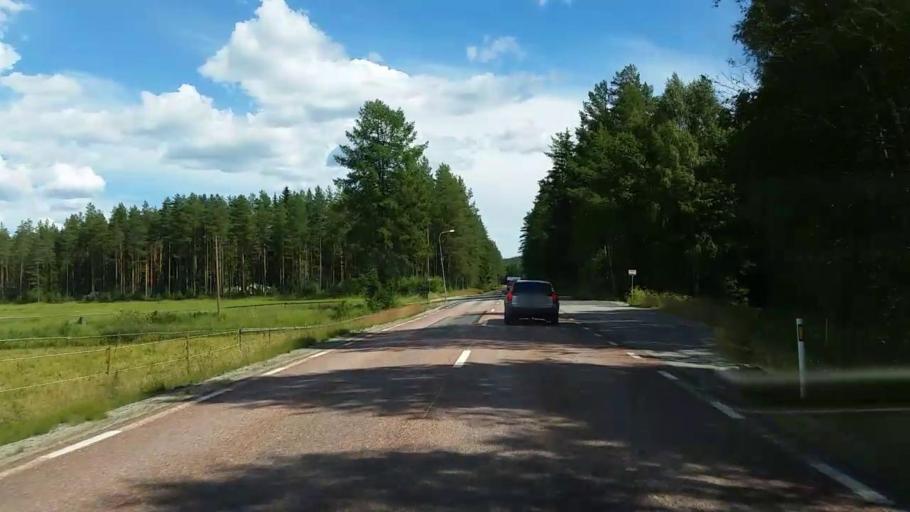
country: SE
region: Gaevleborg
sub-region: Ovanakers Kommun
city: Edsbyn
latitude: 61.3459
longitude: 15.6512
